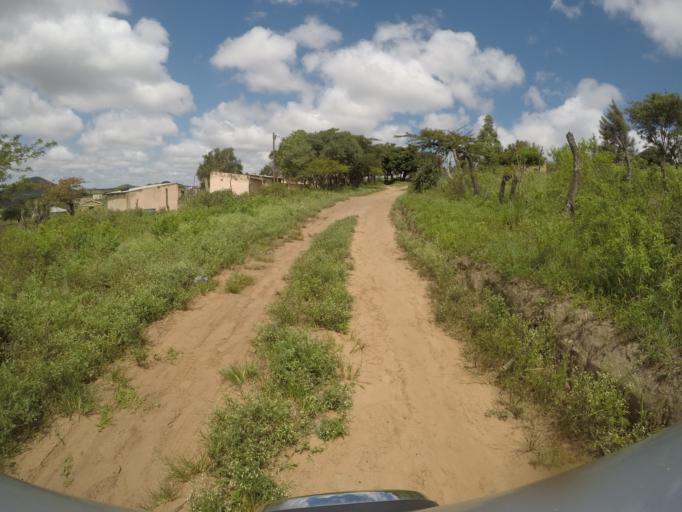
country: ZA
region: KwaZulu-Natal
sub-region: uThungulu District Municipality
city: Empangeni
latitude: -28.5837
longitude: 31.8379
